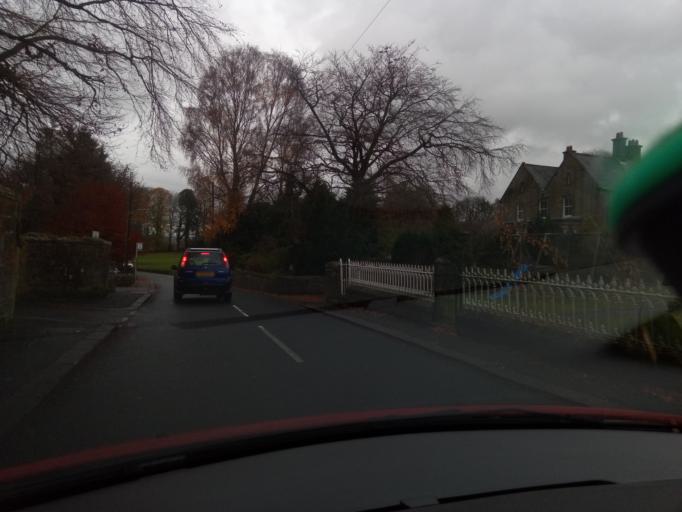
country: GB
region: England
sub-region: Northumberland
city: Birtley
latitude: 55.1438
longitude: -2.2571
